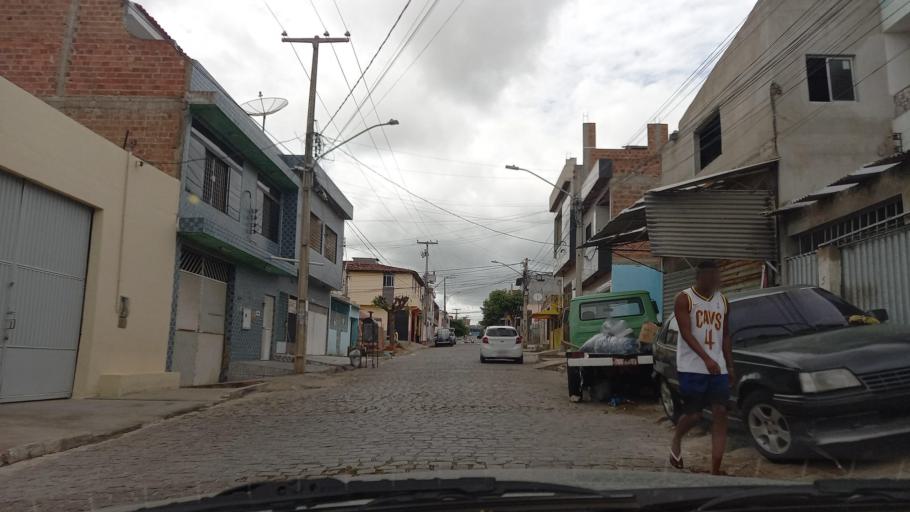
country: BR
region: Pernambuco
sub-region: Caruaru
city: Caruaru
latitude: -8.2710
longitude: -35.9586
